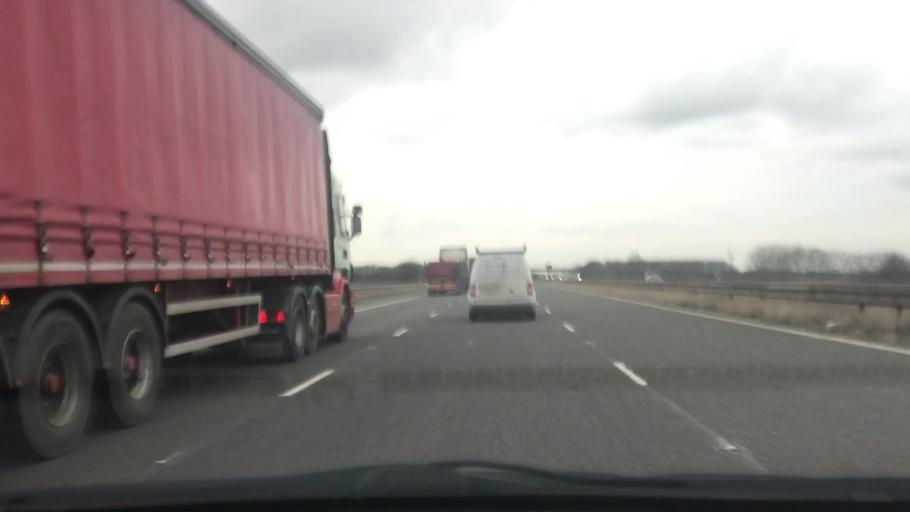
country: GB
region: England
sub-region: Doncaster
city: Hatfield
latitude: 53.5787
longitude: -0.9361
